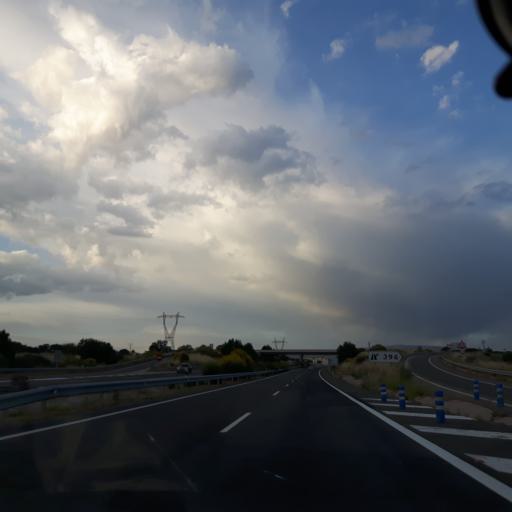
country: ES
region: Castille and Leon
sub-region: Provincia de Salamanca
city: Fuentes de Bejar
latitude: 40.5010
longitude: -5.6760
